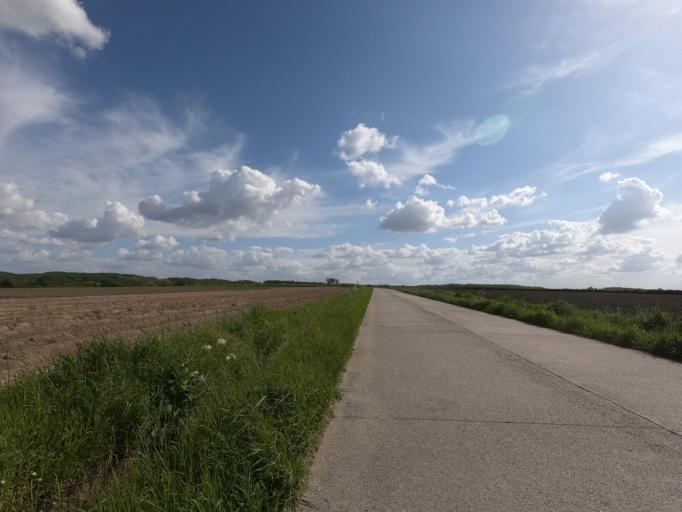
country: BE
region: Flanders
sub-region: Provincie Oost-Vlaanderen
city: Ronse
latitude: 50.7815
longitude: 3.5543
